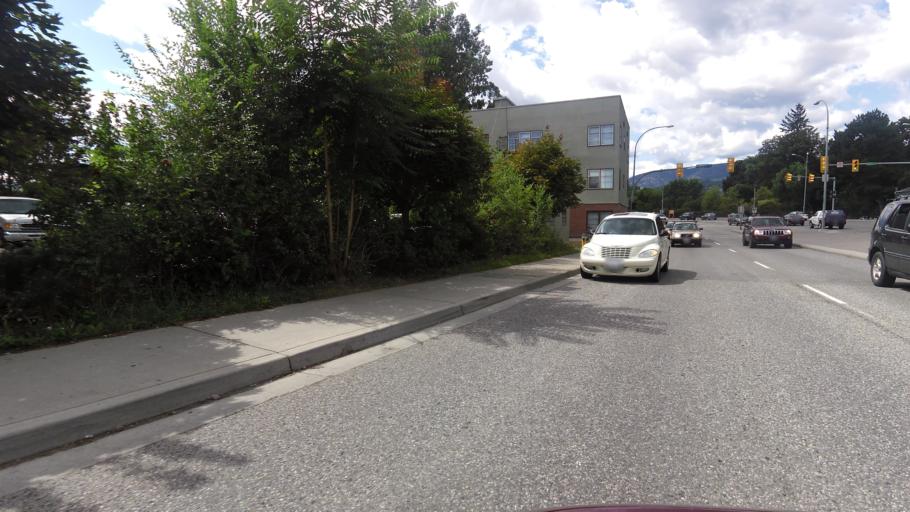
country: CA
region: British Columbia
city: Kelowna
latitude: 49.8835
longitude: -119.4986
